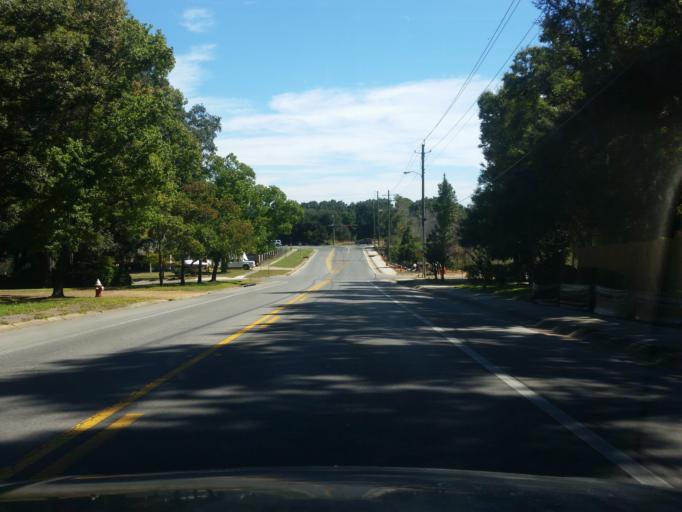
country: US
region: Florida
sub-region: Escambia County
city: East Pensacola Heights
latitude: 30.4810
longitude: -87.1649
